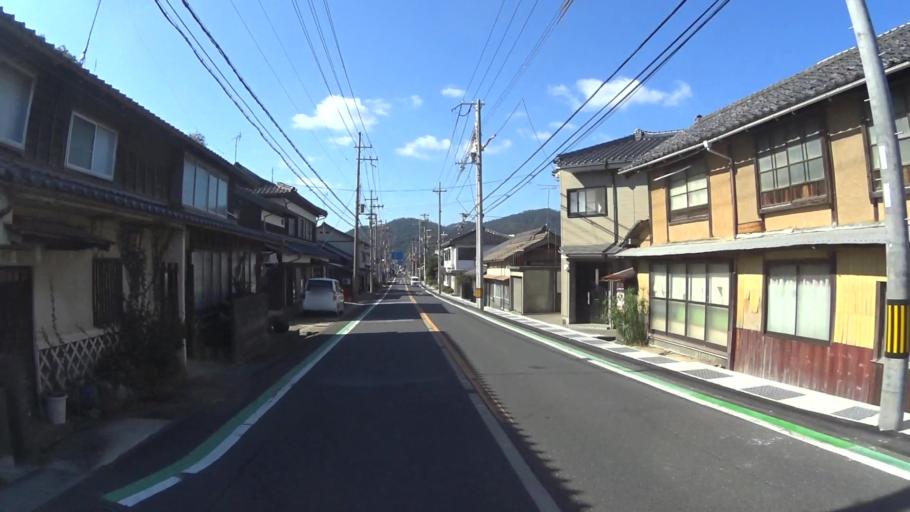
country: JP
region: Kyoto
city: Miyazu
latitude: 35.6818
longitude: 135.0332
